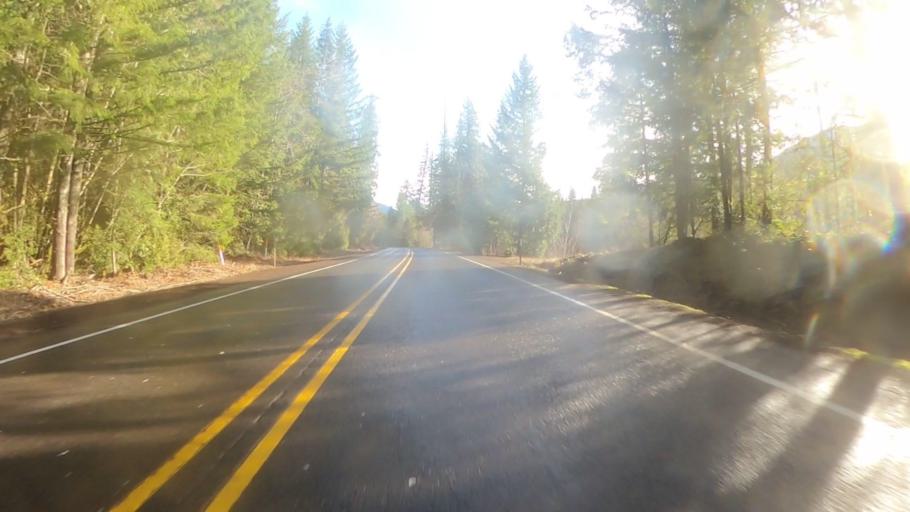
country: US
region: Oregon
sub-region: Lane County
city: Oakridge
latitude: 43.6887
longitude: -122.2580
